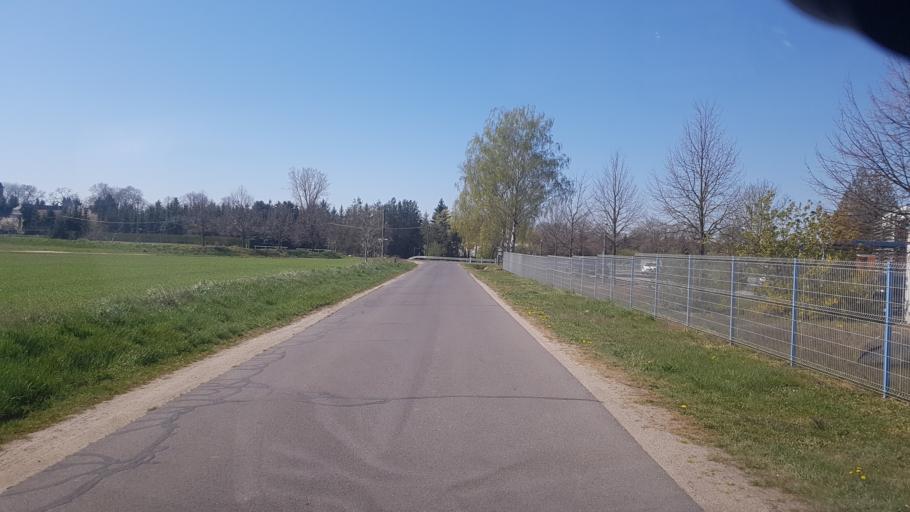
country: DE
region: Brandenburg
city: Sonnewalde
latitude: 51.7143
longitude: 13.6334
